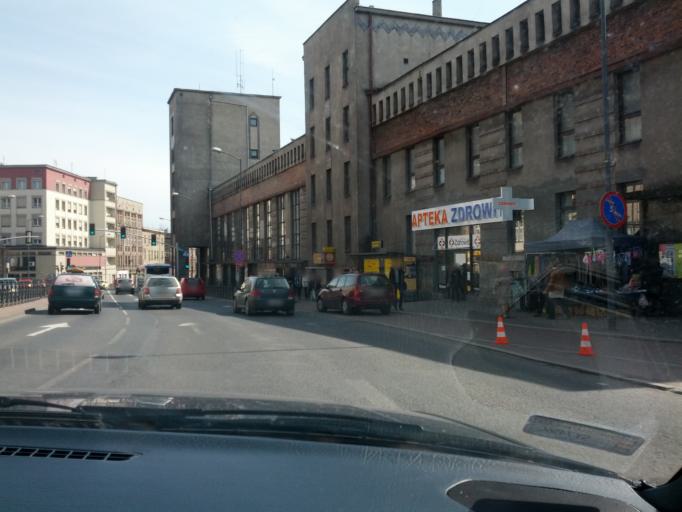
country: PL
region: Silesian Voivodeship
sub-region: Bytom
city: Bytom
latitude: 50.3436
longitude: 18.9143
